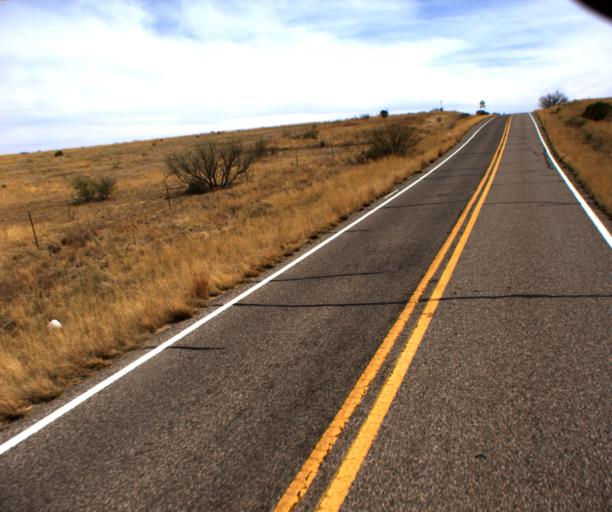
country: US
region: Arizona
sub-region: Cochise County
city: Willcox
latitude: 32.0128
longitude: -109.4401
